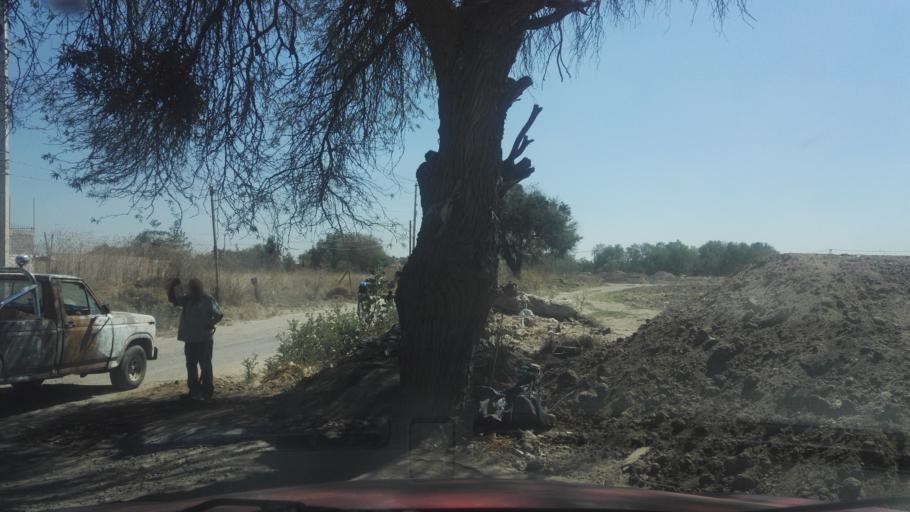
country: MX
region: Guanajuato
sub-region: Leon
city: Fraccionamiento Paraiso Real
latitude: 21.0876
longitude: -101.5920
